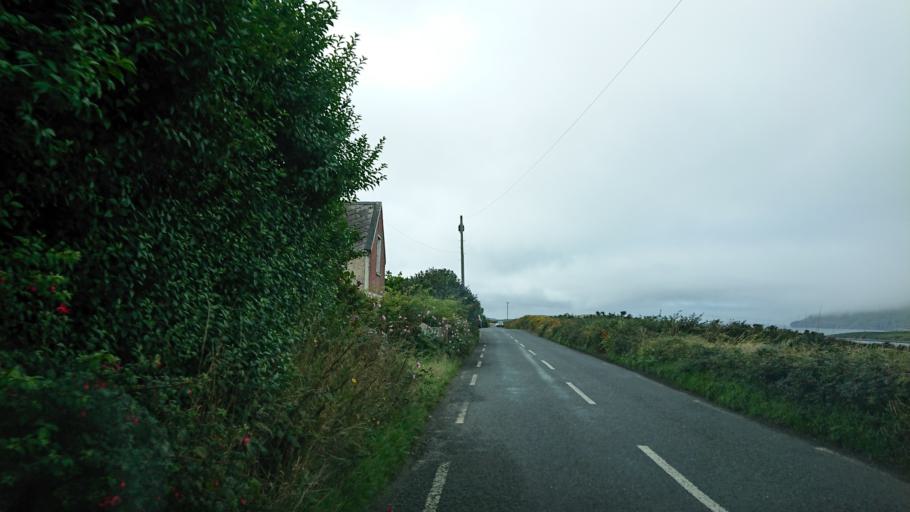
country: IE
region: Munster
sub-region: Ciarrai
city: Cahersiveen
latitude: 51.9329
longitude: -10.2579
